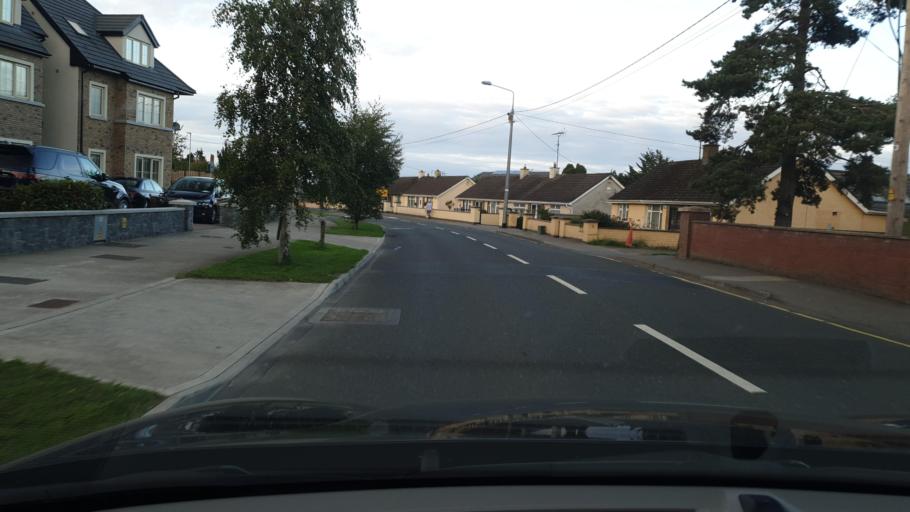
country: IE
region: Leinster
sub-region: South Dublin
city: Rathcoole
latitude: 53.2787
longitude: -6.4780
